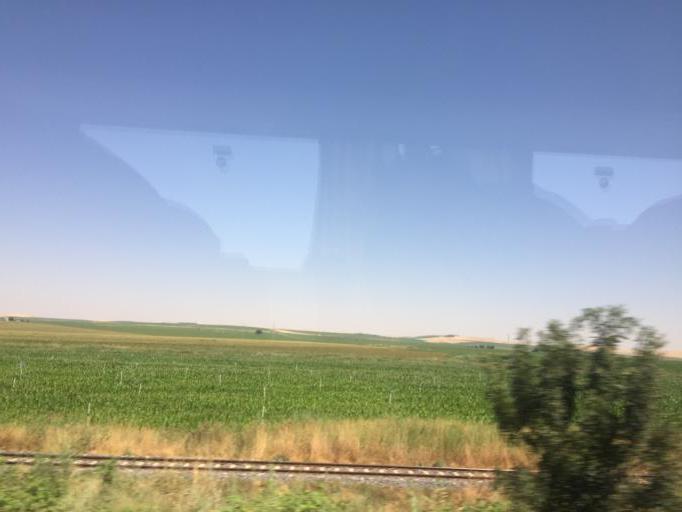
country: TR
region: Diyarbakir
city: Tepe
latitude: 37.8508
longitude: 40.7665
